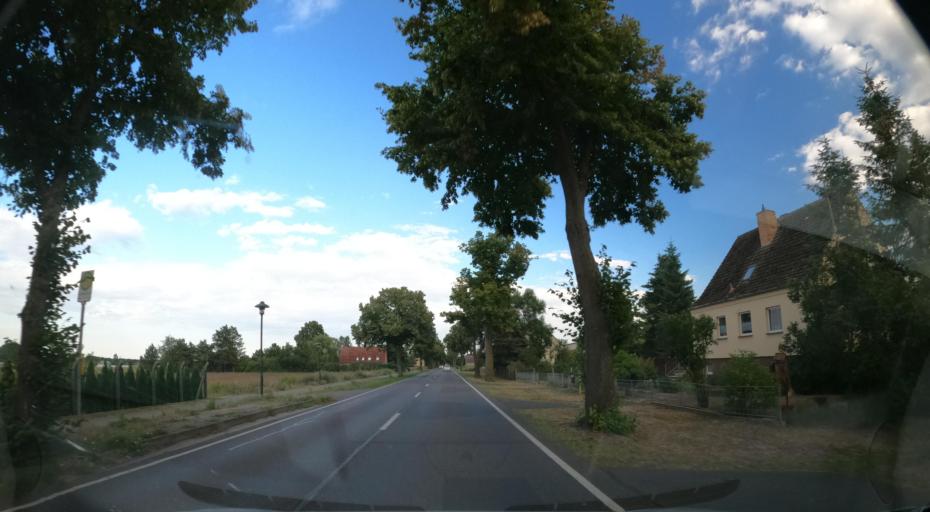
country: DE
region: Brandenburg
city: Brussow
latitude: 53.4599
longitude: 14.1852
